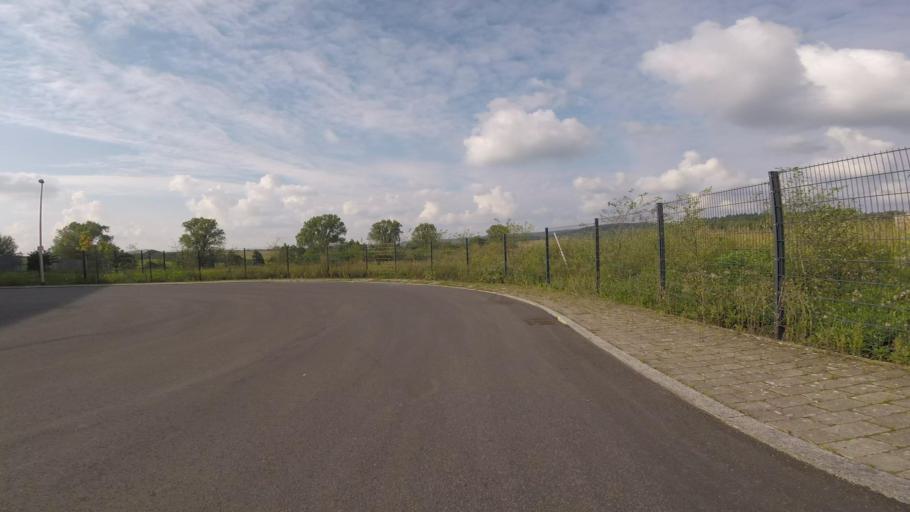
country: DE
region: Baden-Wuerttemberg
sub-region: Regierungsbezirk Stuttgart
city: Aspach
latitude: 48.9648
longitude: 9.4217
